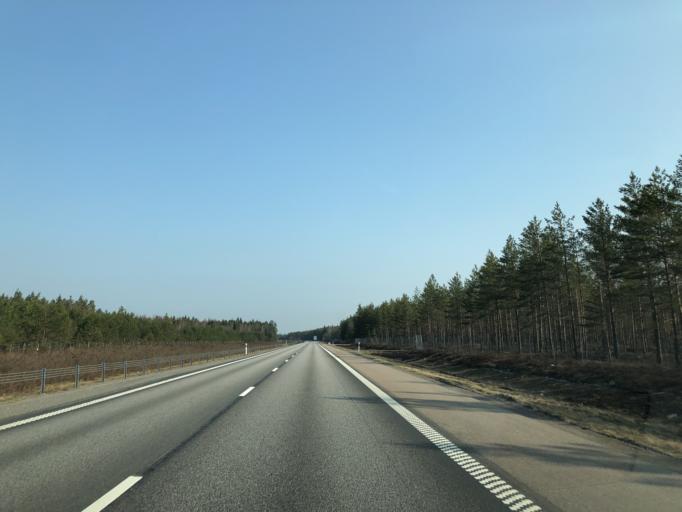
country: SE
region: Joenkoeping
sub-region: Vaggeryds Kommun
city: Skillingaryd
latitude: 57.3156
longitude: 14.0973
